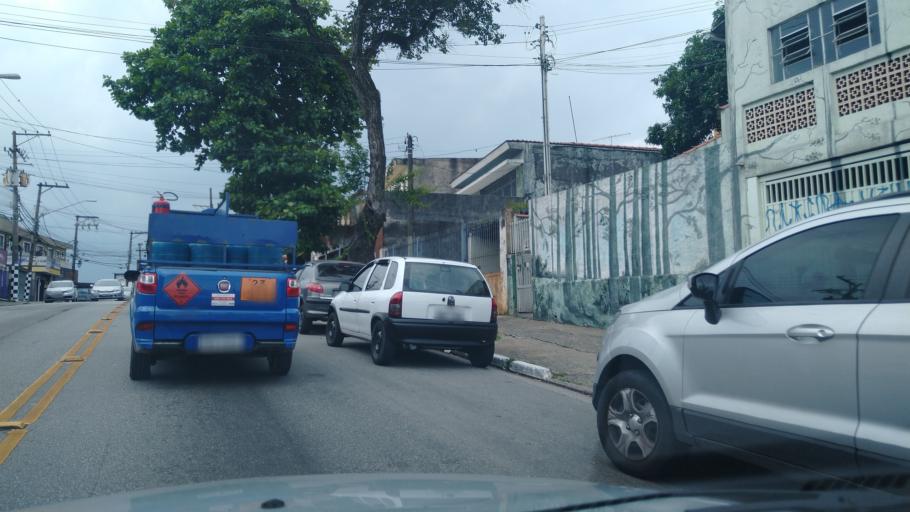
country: BR
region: Sao Paulo
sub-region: Osasco
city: Osasco
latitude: -23.5071
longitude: -46.7605
